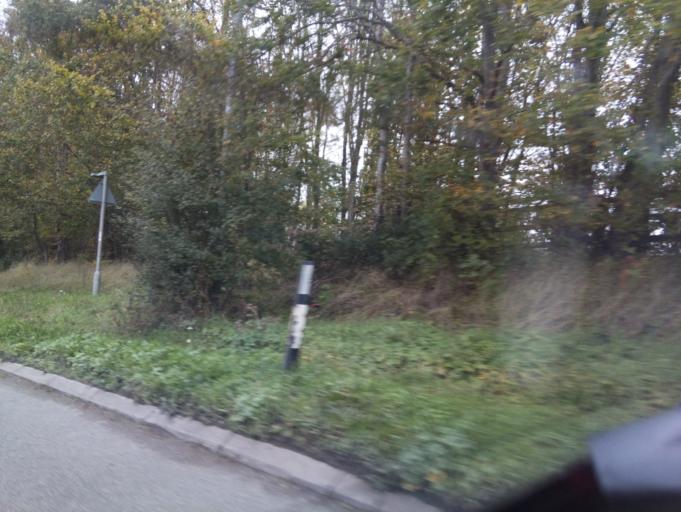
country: GB
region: England
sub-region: Somerset
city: Creech Saint Michael
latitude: 51.0168
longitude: -3.0555
